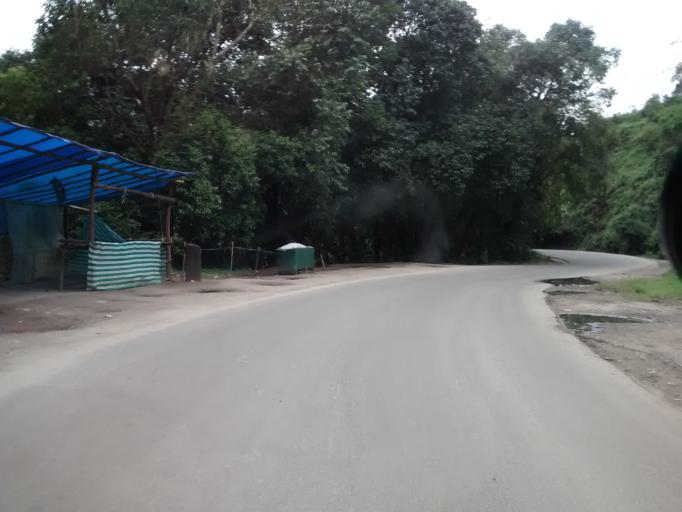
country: IN
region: Kerala
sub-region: Idukki
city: Munnar
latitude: 10.1179
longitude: 77.1506
